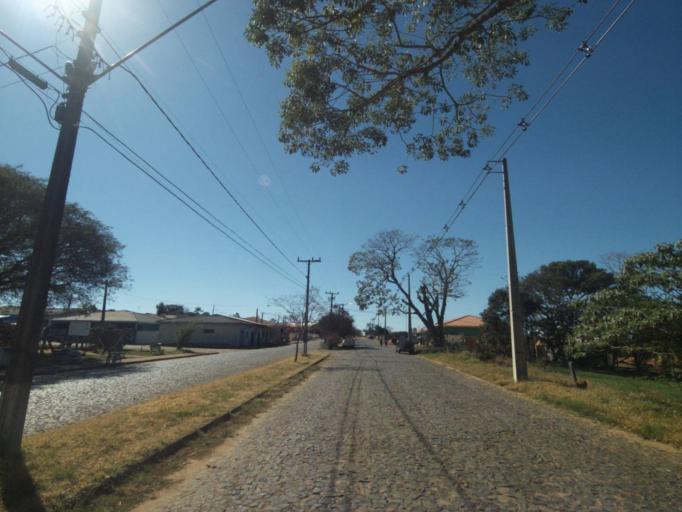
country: BR
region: Parana
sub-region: Reserva
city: Reserva
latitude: -24.6247
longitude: -50.6417
